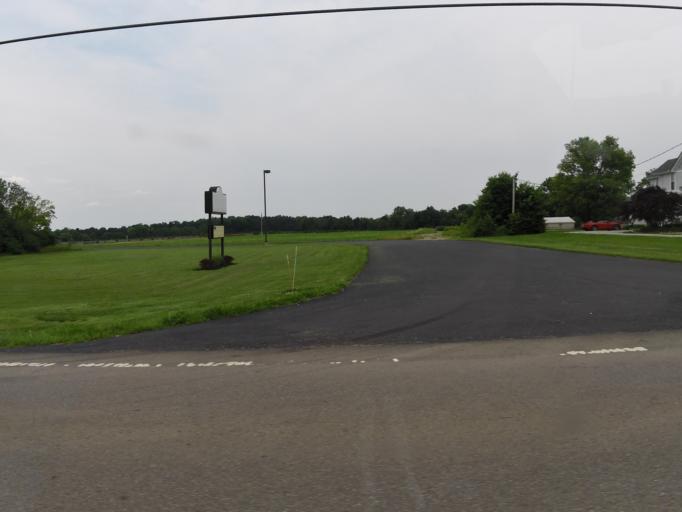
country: US
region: Ohio
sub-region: Warren County
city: Waynesville
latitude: 39.5191
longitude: -84.0548
